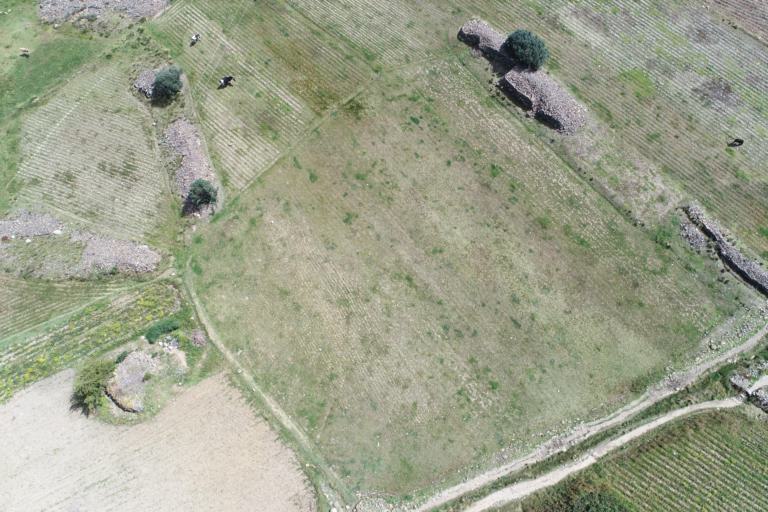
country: BO
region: La Paz
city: Achacachi
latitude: -16.0192
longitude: -68.6171
